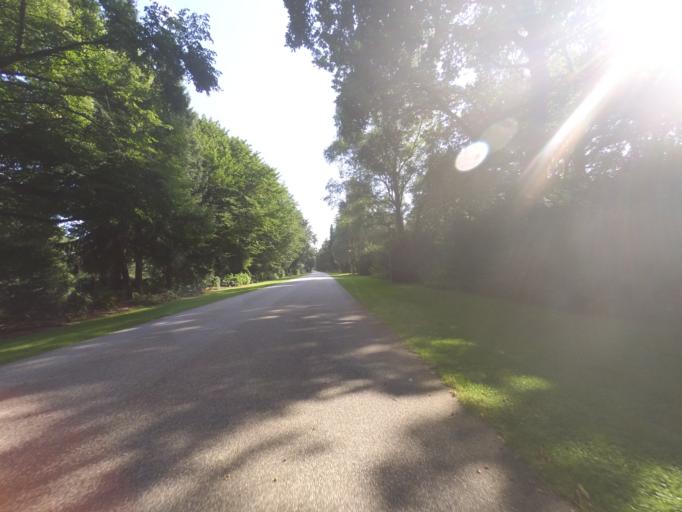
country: DE
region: Hamburg
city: Wandsbek
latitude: 53.5568
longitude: 10.1322
